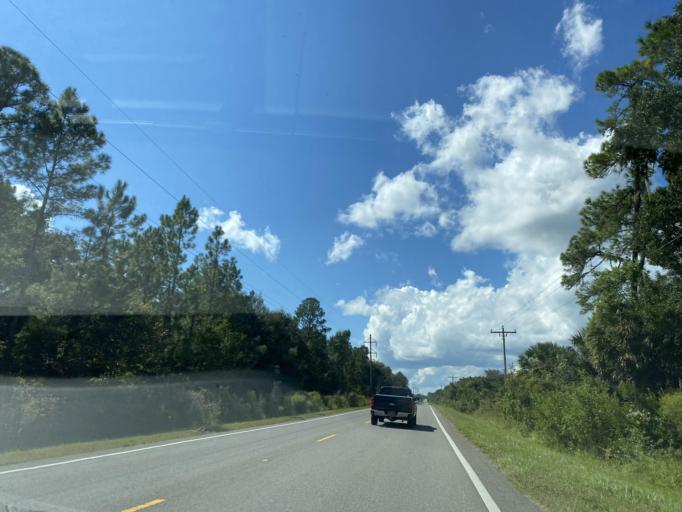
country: US
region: Florida
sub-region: Lake County
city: Umatilla
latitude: 28.9603
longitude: -81.6049
